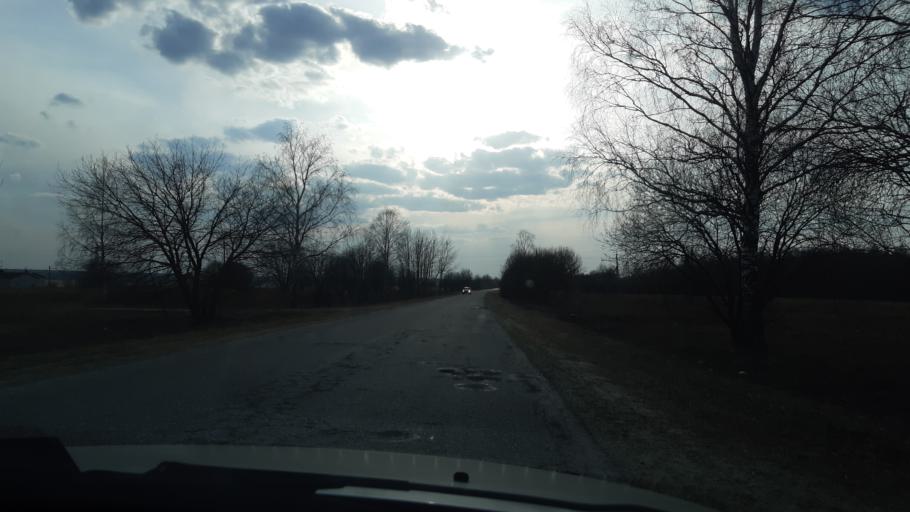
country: RU
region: Vladimir
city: Nikologory
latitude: 56.0978
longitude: 41.9560
